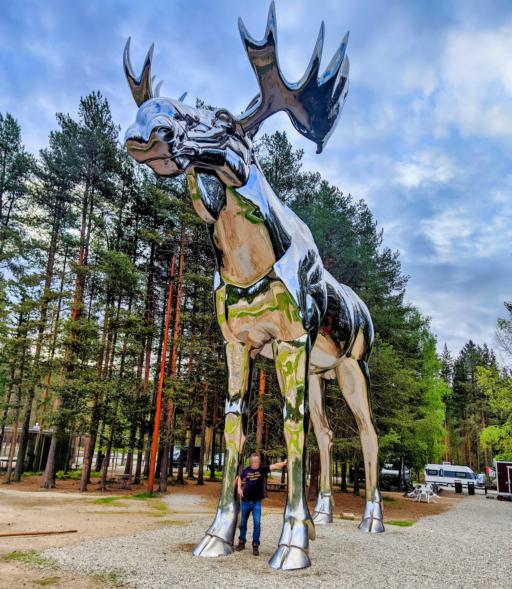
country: NO
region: Hedmark
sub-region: Stor-Elvdal
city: Koppang
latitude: 61.6679
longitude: 10.8842
